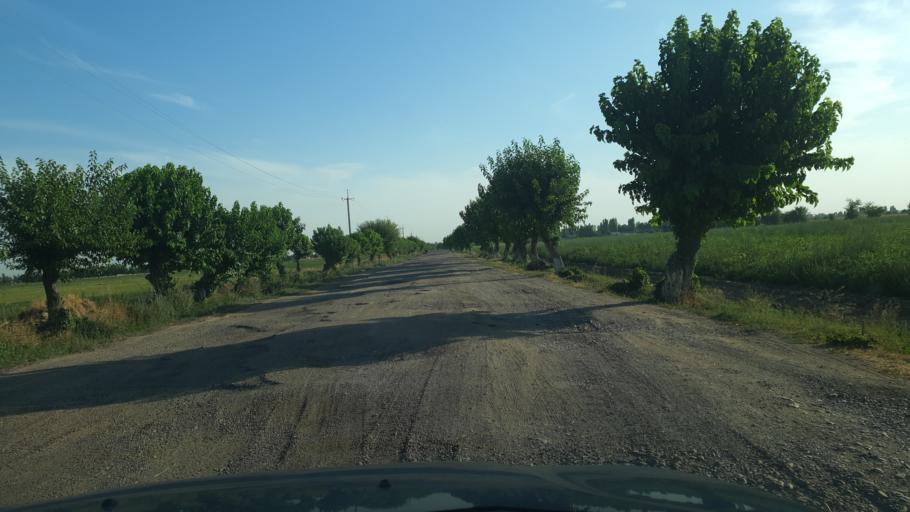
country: UZ
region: Toshkent
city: Tuytepa
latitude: 41.0949
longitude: 69.3724
